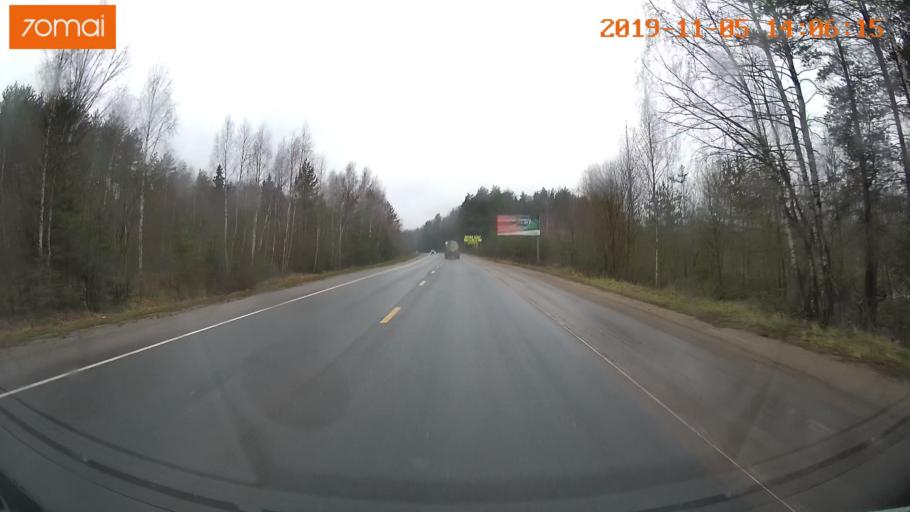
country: RU
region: Ivanovo
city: Kokhma
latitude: 56.9980
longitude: 41.1425
